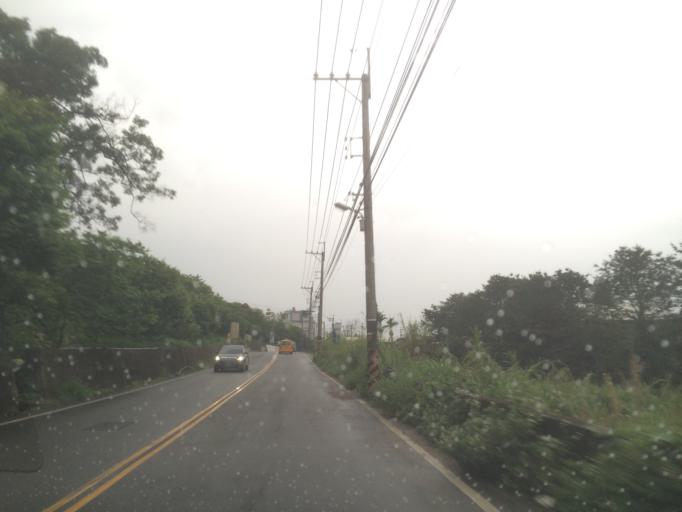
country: TW
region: Taiwan
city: Fengyuan
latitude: 24.1832
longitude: 120.8159
